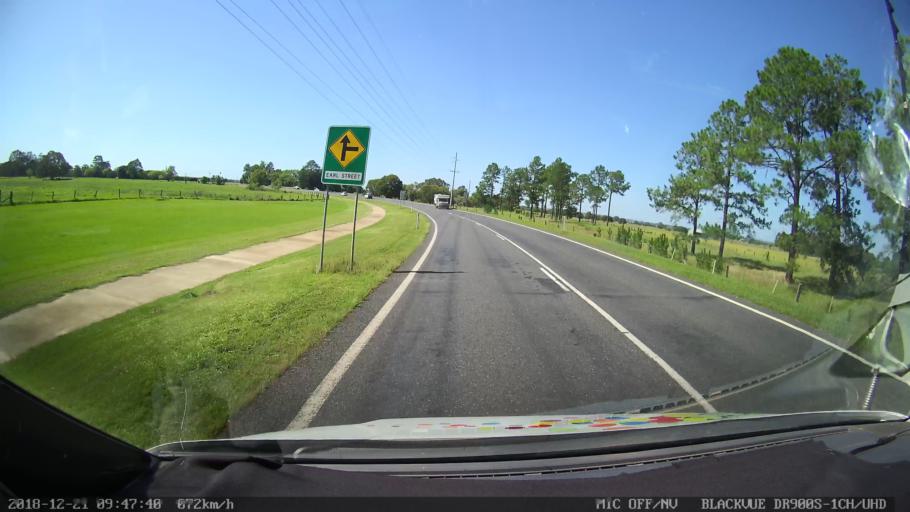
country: AU
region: New South Wales
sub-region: Clarence Valley
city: Grafton
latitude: -29.6475
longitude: 152.9270
